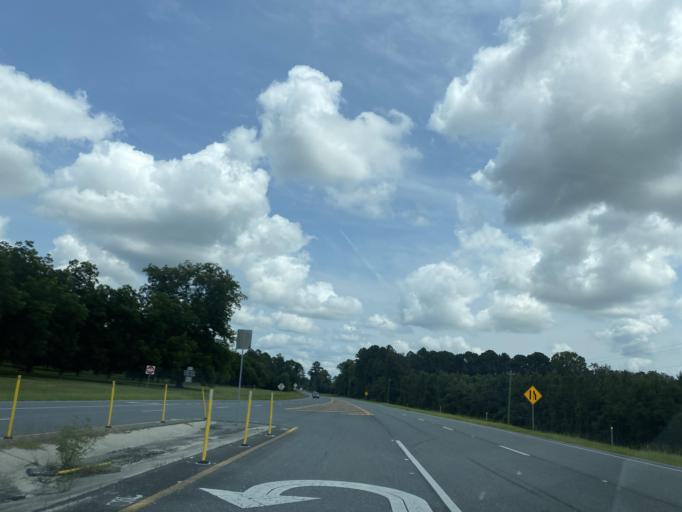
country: US
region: Georgia
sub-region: Ware County
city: Deenwood
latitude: 31.2894
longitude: -82.4460
